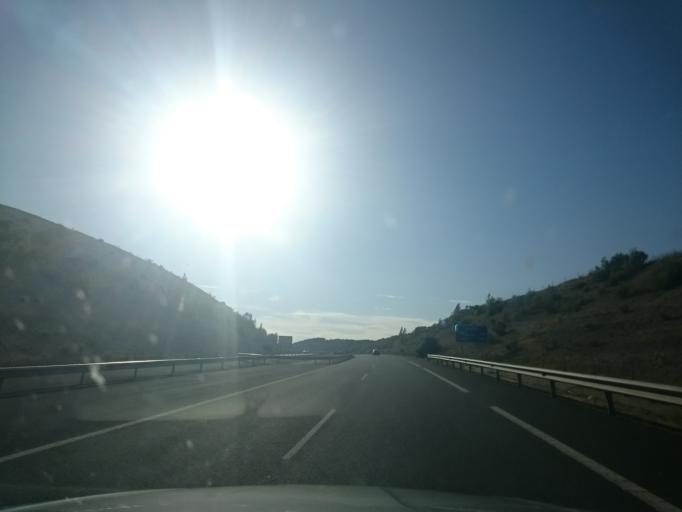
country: ES
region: Castille and Leon
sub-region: Provincia de Burgos
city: Villanueva de Argano
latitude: 42.3785
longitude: -3.9365
